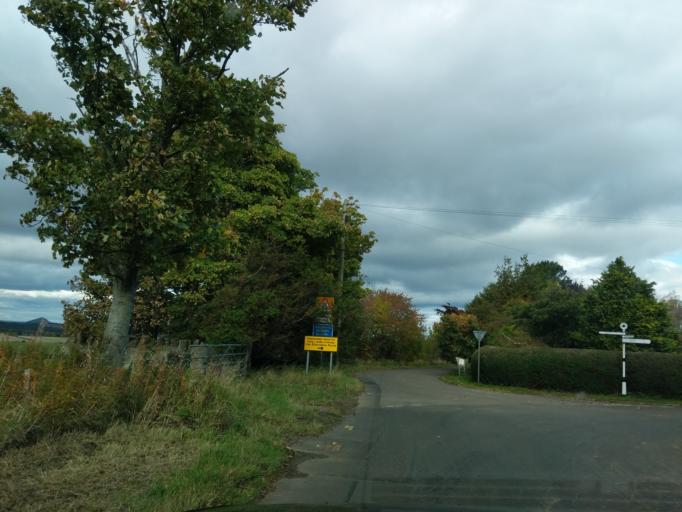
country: GB
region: Scotland
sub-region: East Lothian
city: Haddington
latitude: 55.9371
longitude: -2.7175
